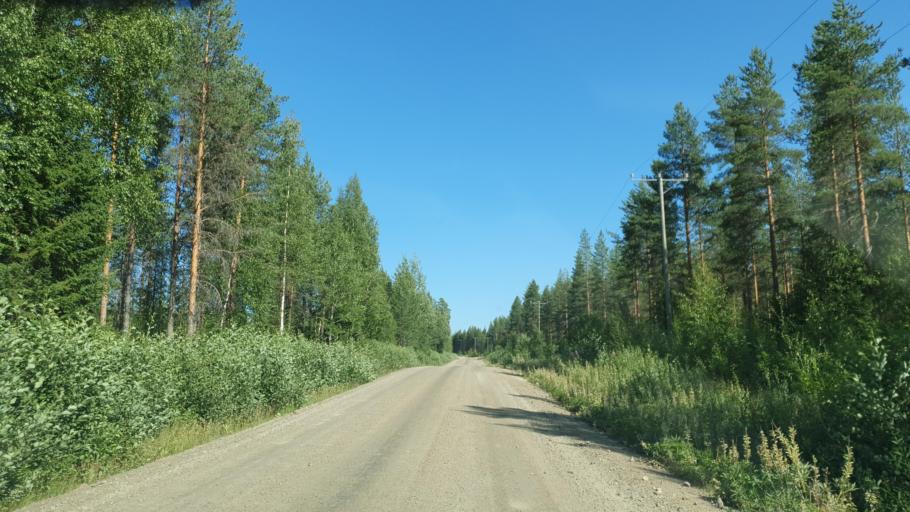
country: FI
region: Kainuu
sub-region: Kehys-Kainuu
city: Kuhmo
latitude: 64.0526
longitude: 29.5717
